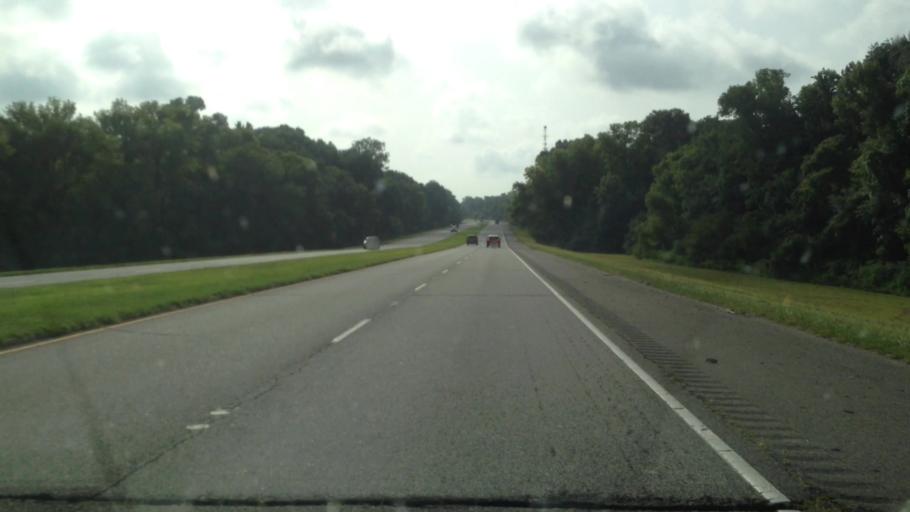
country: US
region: Louisiana
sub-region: Saint Landry Parish
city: Krotz Springs
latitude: 30.5402
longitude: -91.7772
